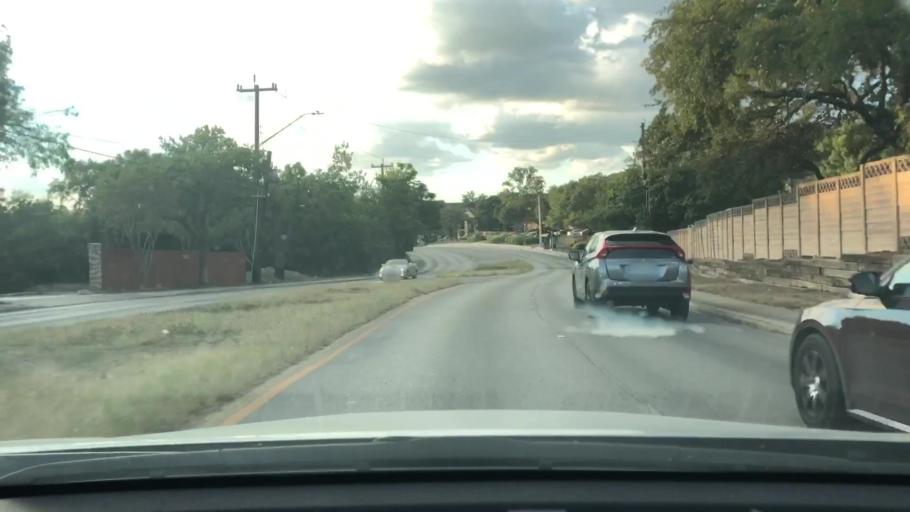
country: US
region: Texas
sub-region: Bexar County
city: Hollywood Park
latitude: 29.5558
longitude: -98.4718
